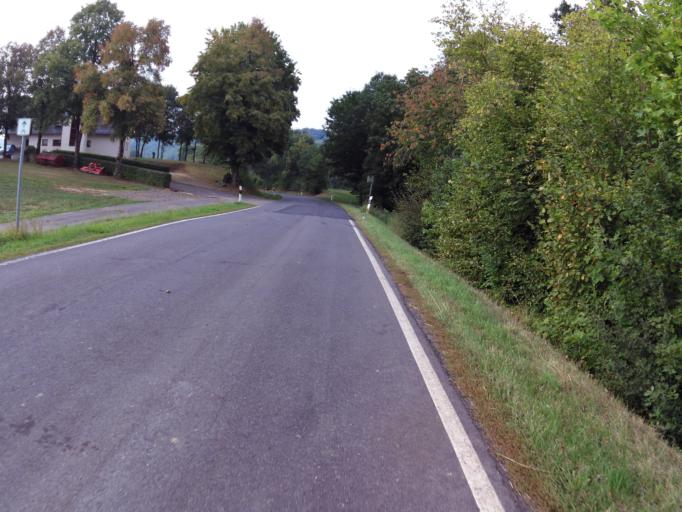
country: DE
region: Rheinland-Pfalz
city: Wilsecker
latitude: 50.0108
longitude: 6.5701
